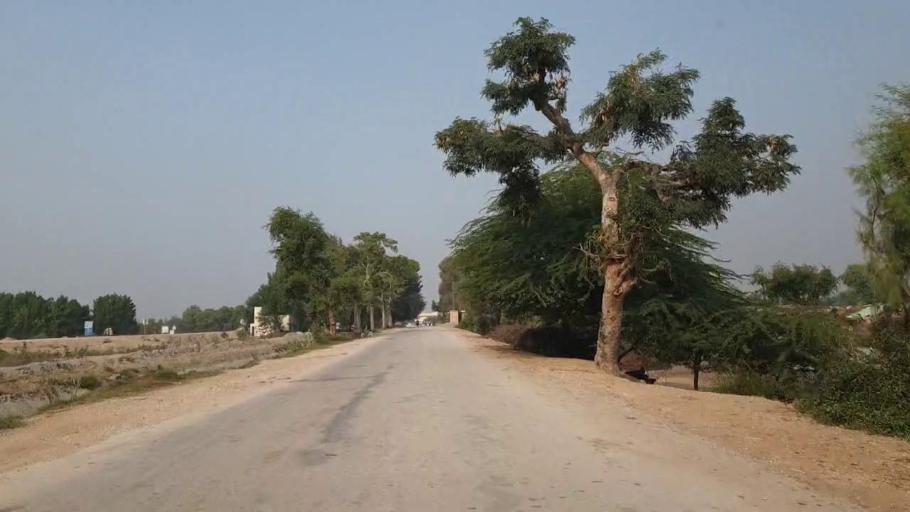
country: PK
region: Sindh
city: Bhan
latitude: 26.5857
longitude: 67.7292
